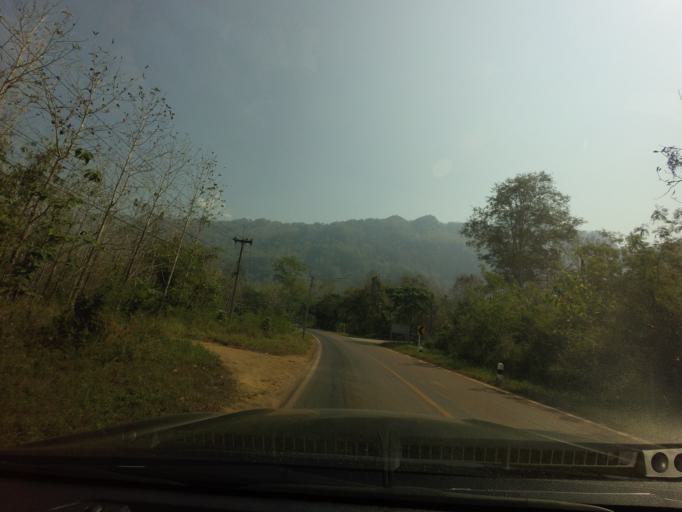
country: TH
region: Kanchanaburi
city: Thong Pha Phum
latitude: 14.6555
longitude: 98.6027
